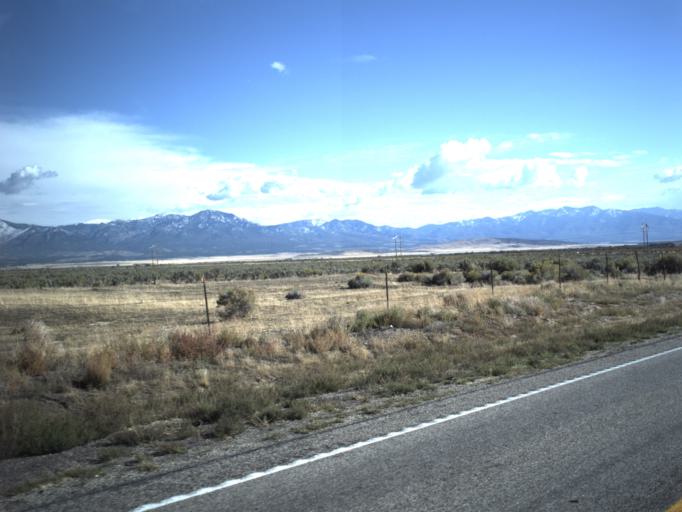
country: US
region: Utah
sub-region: Millard County
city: Fillmore
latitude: 39.1601
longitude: -112.4100
